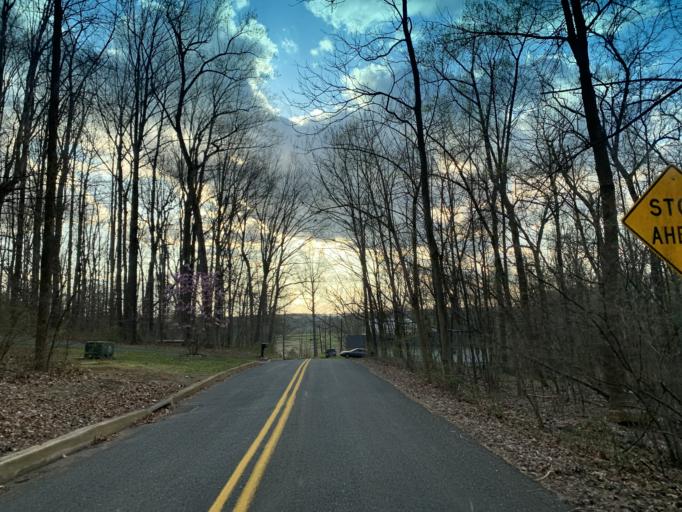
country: US
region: Maryland
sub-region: Harford County
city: South Bel Air
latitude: 39.6144
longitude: -76.3031
